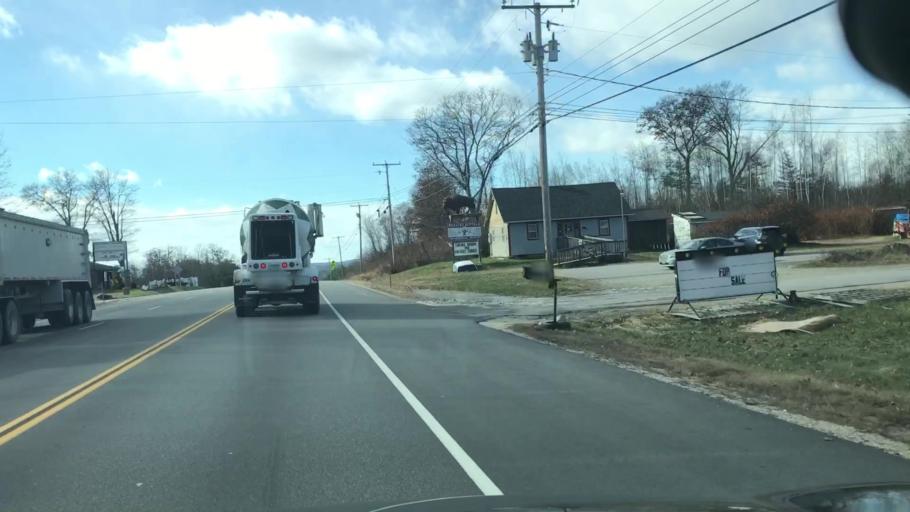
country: US
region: New Hampshire
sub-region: Merrimack County
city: Chichester
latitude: 43.2478
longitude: -71.4239
